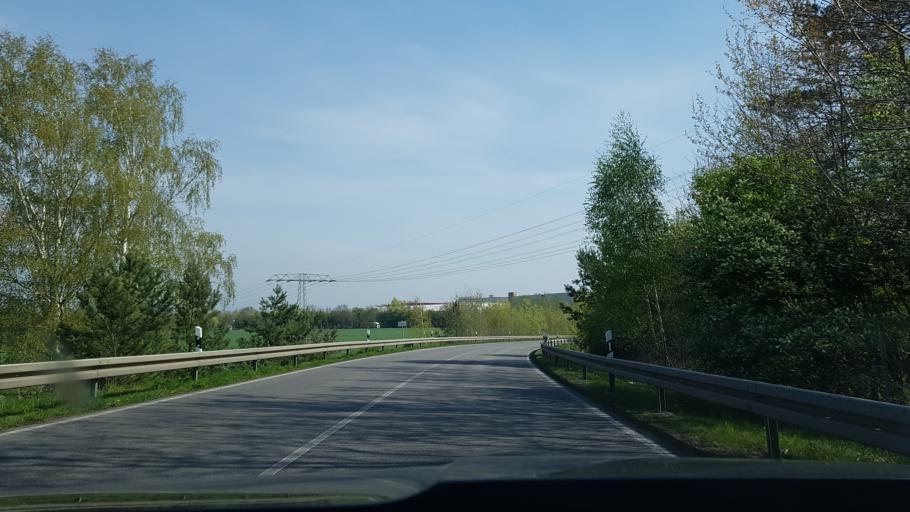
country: DE
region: Brandenburg
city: Lubbenau
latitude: 51.8419
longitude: 13.9443
